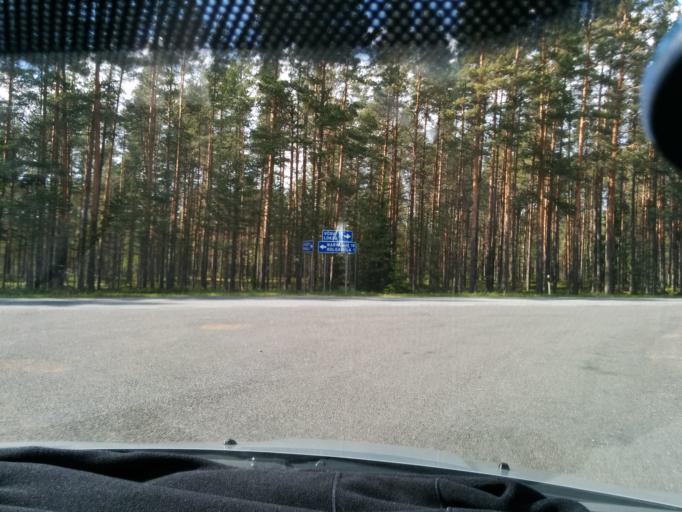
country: EE
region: Harju
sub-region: Loksa linn
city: Loksa
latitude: 59.5354
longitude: 25.7282
